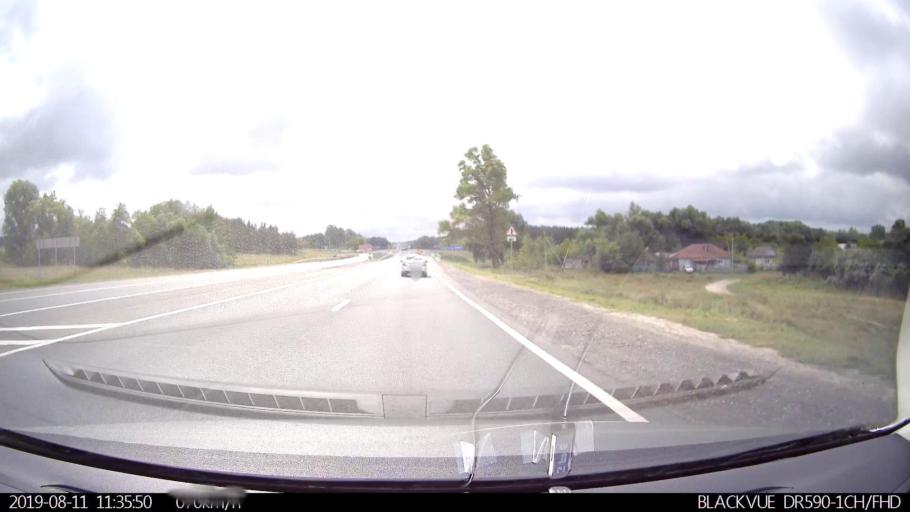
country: RU
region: Ulyanovsk
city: Silikatnyy
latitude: 54.0023
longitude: 48.2208
